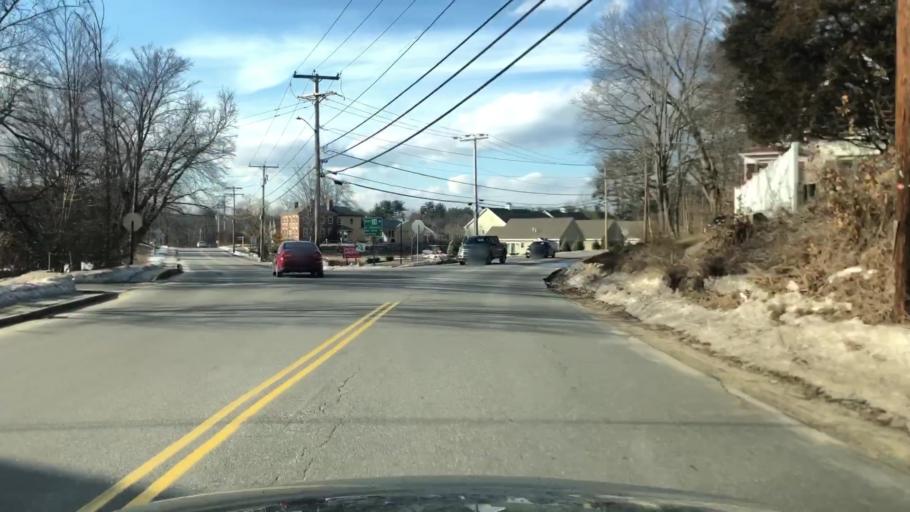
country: US
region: New Hampshire
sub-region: Hillsborough County
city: Milford
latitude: 42.8408
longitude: -71.6575
